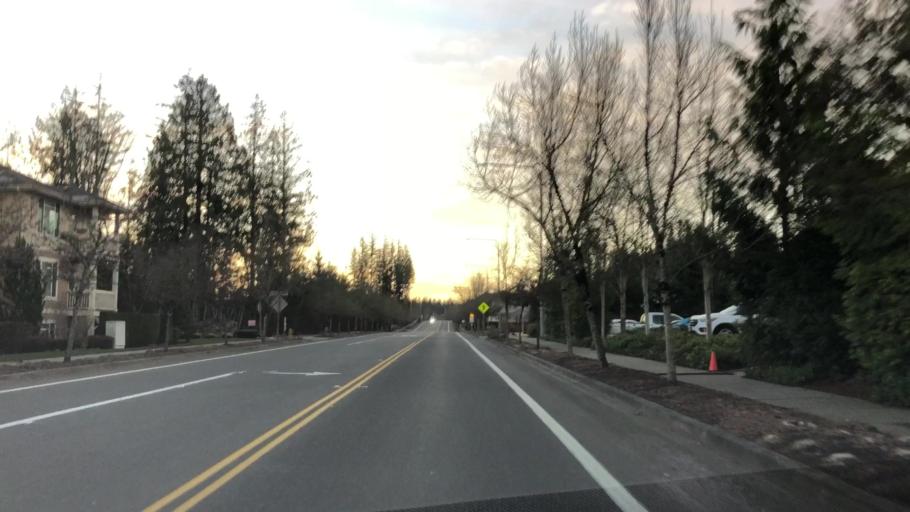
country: US
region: Washington
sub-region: King County
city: Union Hill-Novelty Hill
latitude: 47.7010
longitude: -122.0213
